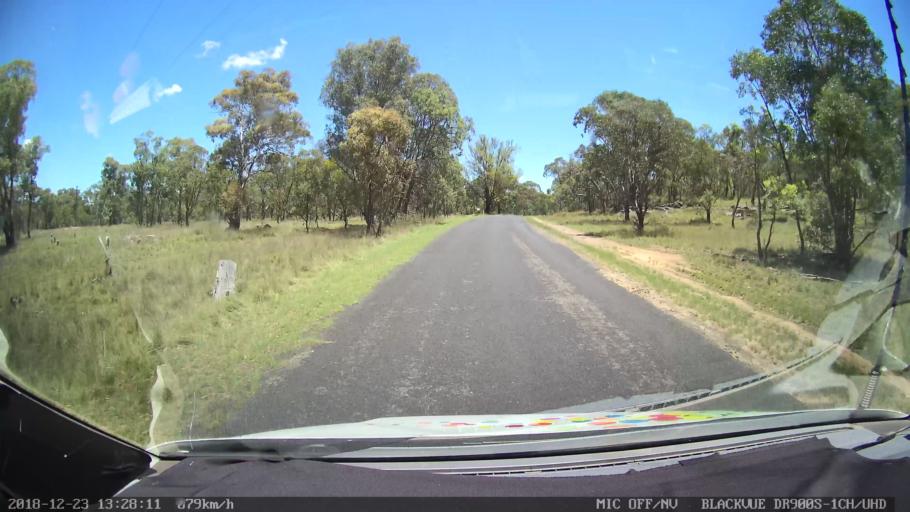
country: AU
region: New South Wales
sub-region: Armidale Dumaresq
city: Armidale
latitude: -30.4650
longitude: 151.3516
